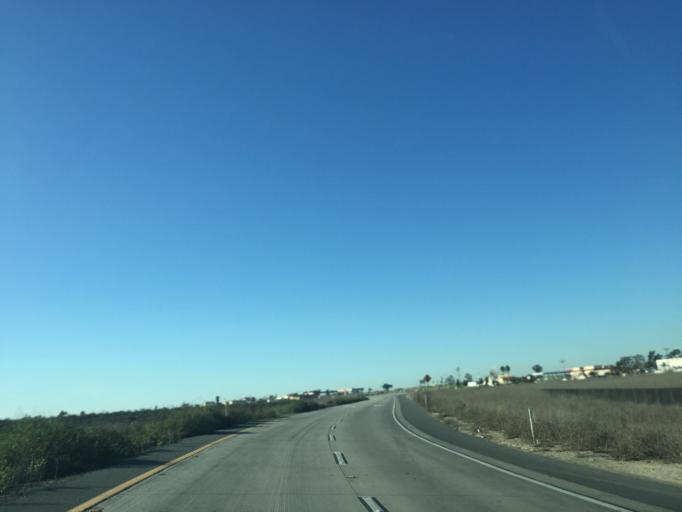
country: MX
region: Baja California
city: Tijuana
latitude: 32.5648
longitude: -116.9584
